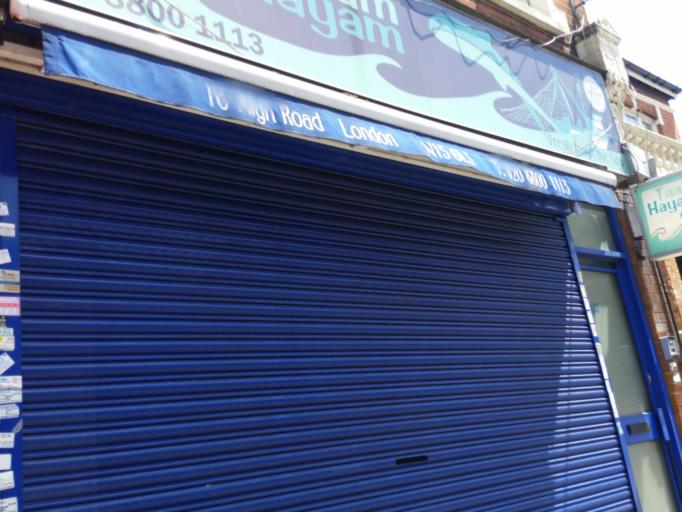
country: GB
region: England
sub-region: Greater London
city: Harringay
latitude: 51.5761
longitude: -0.0725
